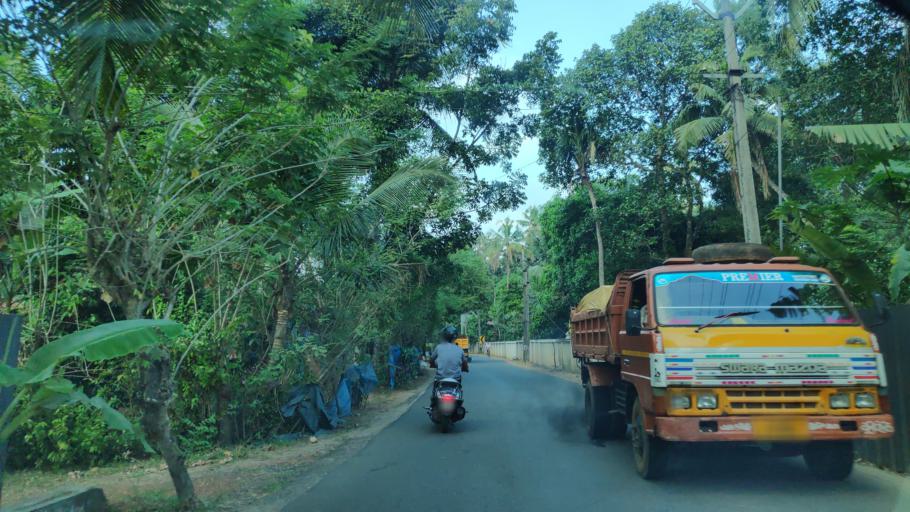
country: IN
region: Kerala
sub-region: Alappuzha
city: Shertallai
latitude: 9.6698
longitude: 76.3885
